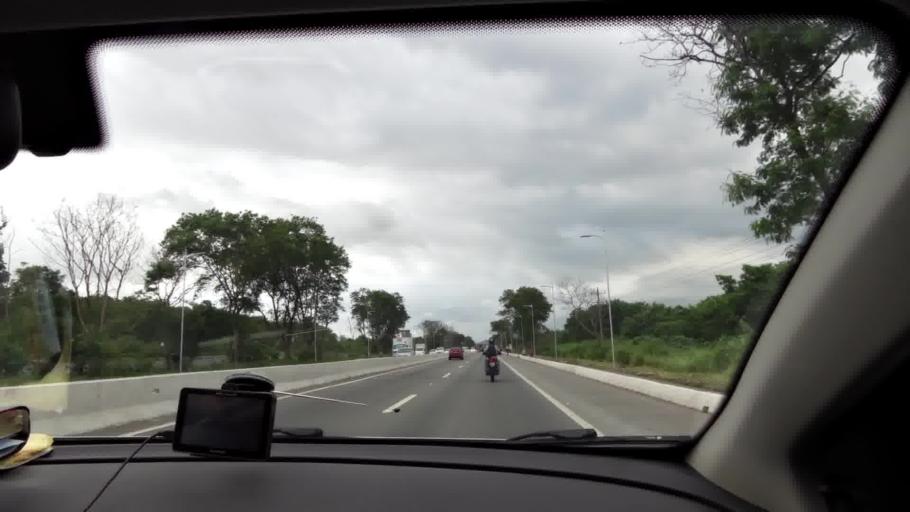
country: BR
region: Espirito Santo
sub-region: Vila Velha
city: Vila Velha
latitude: -20.2461
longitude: -40.2835
